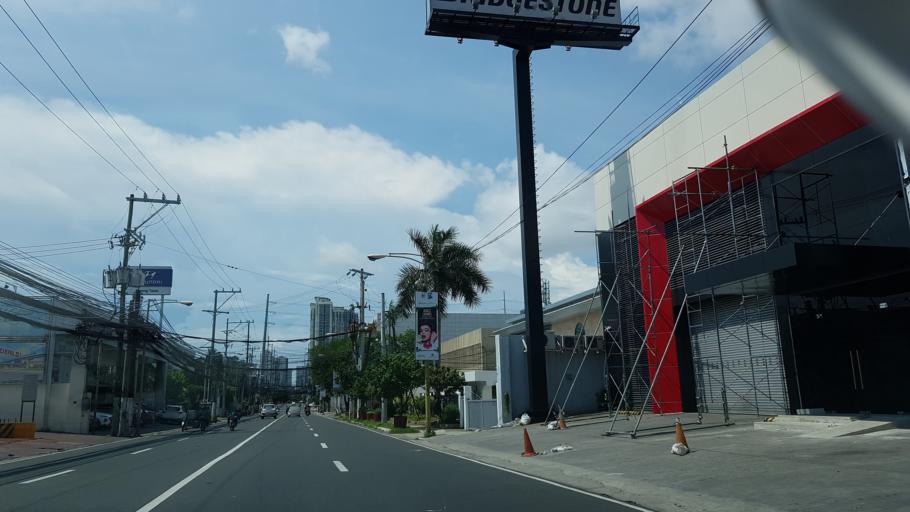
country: PH
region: Metro Manila
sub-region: Makati City
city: Makati City
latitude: 14.5351
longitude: 121.0216
